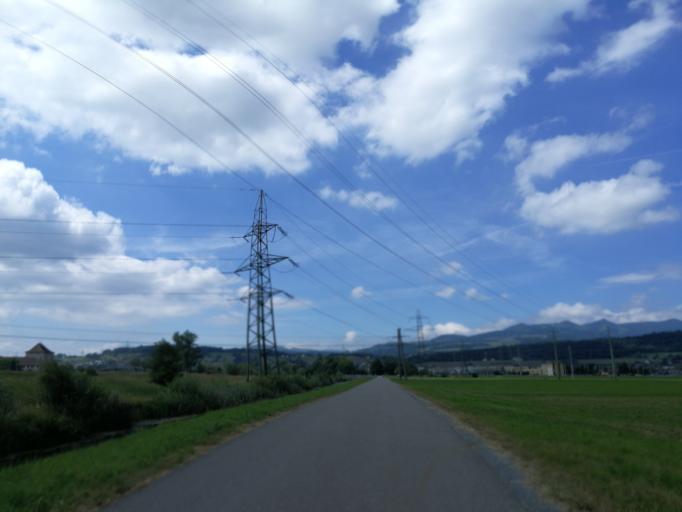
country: CH
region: Saint Gallen
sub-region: Wahlkreis See-Gaster
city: Uznach
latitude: 47.2144
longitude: 8.9748
